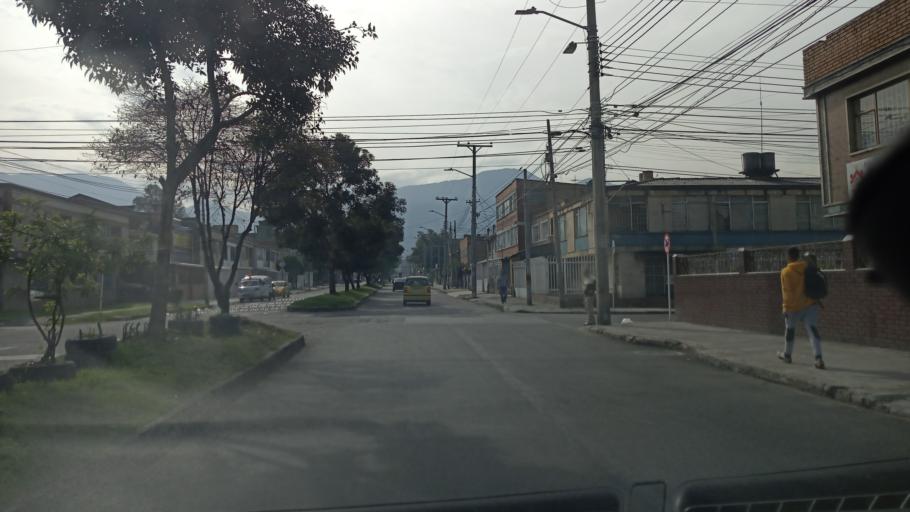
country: CO
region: Bogota D.C.
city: Bogota
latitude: 4.5816
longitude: -74.0999
